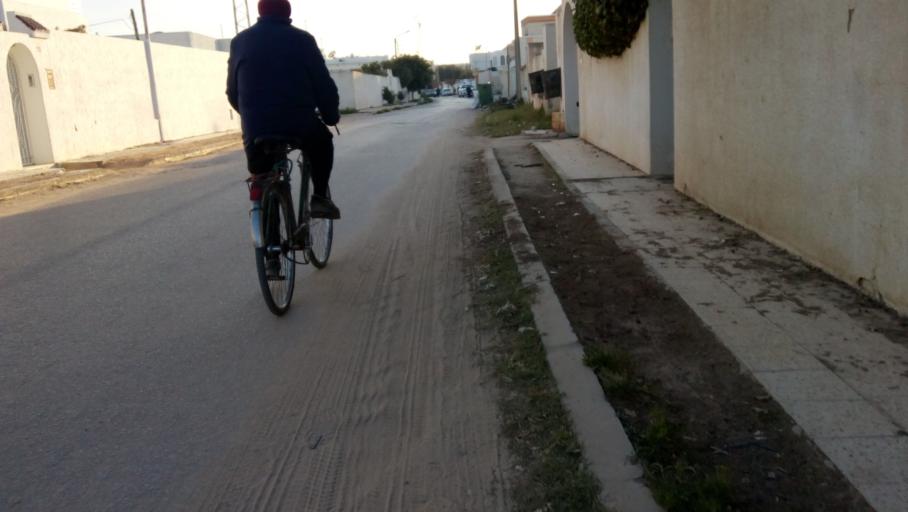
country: TN
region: Safaqis
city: Sfax
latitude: 34.7507
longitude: 10.7361
